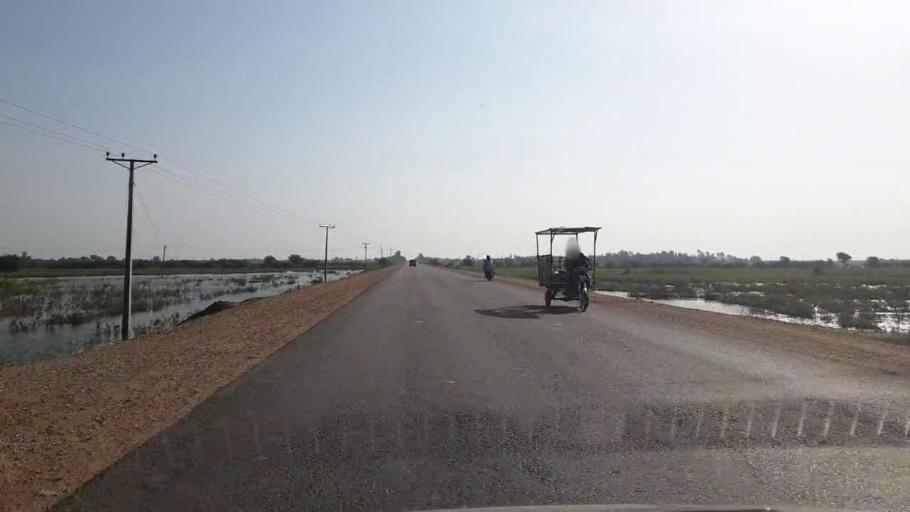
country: PK
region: Sindh
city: Badin
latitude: 24.6582
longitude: 68.9637
